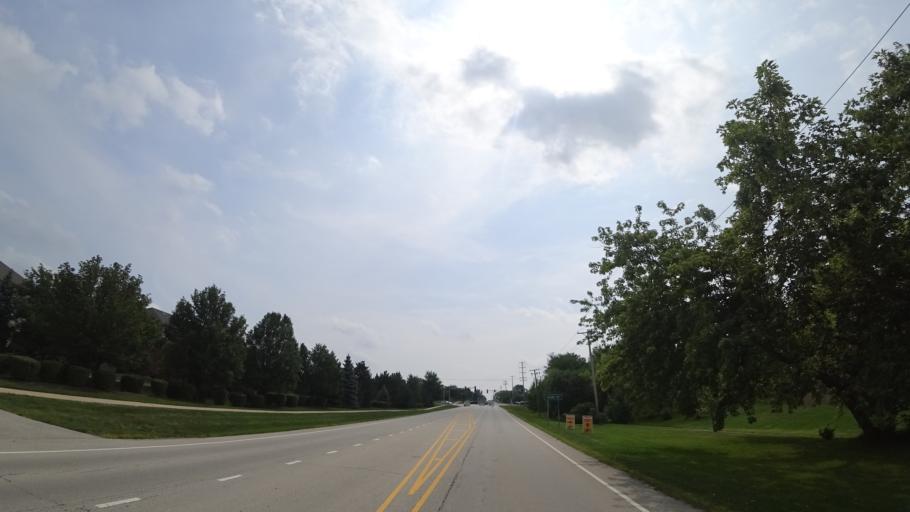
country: US
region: Illinois
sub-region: Will County
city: Goodings Grove
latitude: 41.6309
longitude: -87.9116
